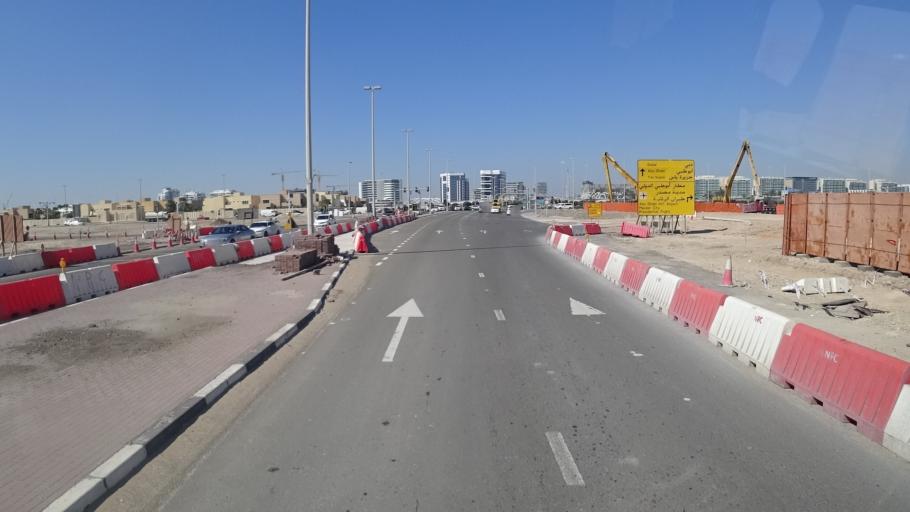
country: AE
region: Abu Dhabi
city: Abu Dhabi
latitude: 24.4395
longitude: 54.6018
